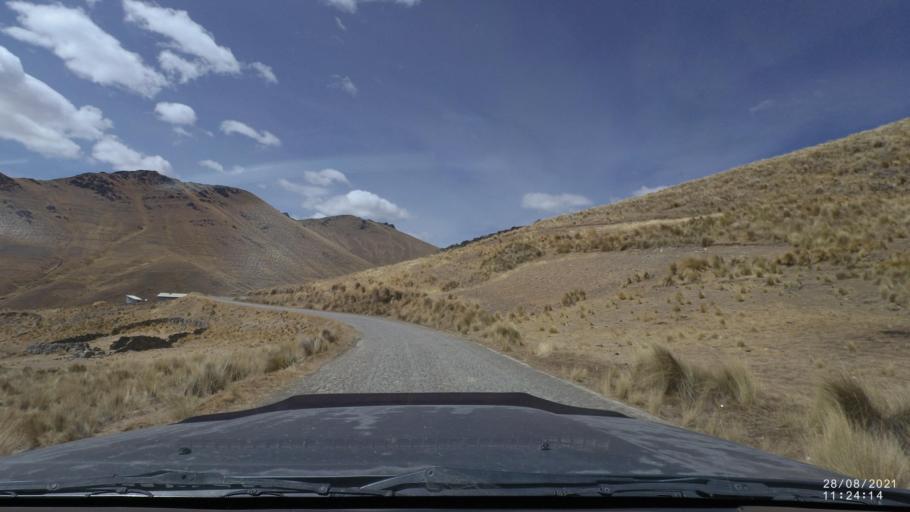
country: BO
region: Cochabamba
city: Sipe Sipe
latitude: -17.1660
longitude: -66.3519
